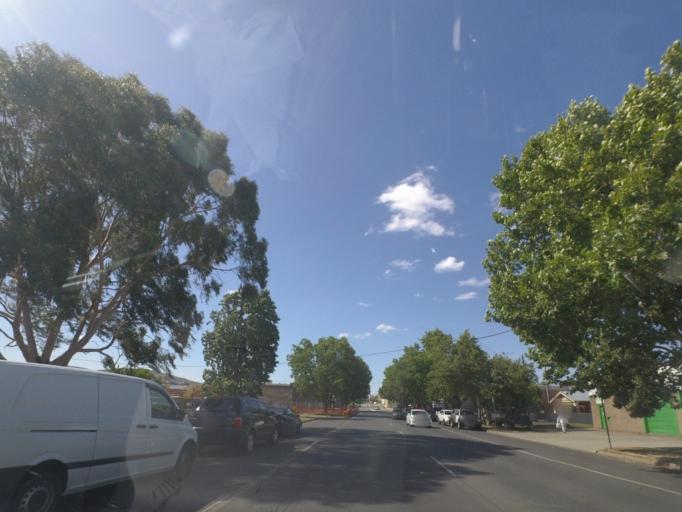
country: AU
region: New South Wales
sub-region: Albury Municipality
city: South Albury
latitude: -36.0863
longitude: 146.9146
